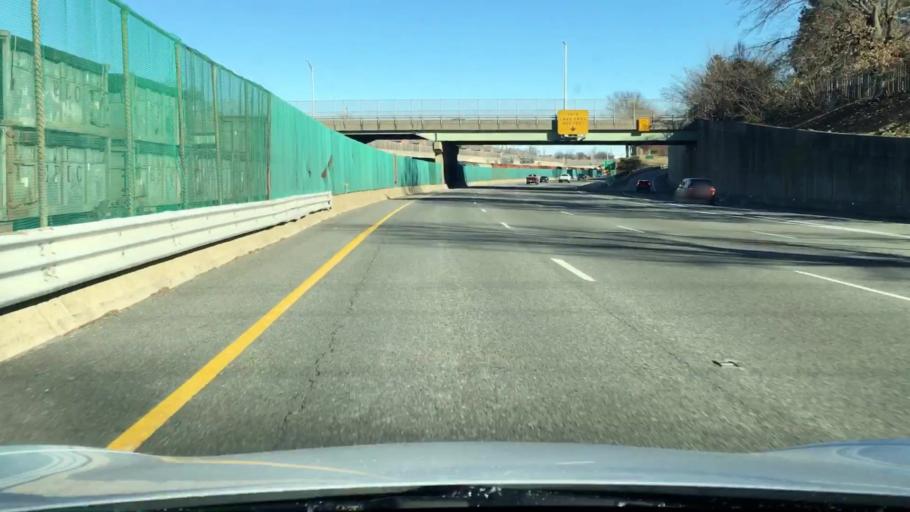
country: US
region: Virginia
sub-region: City of Richmond
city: Richmond
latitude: 37.5593
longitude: -77.4889
